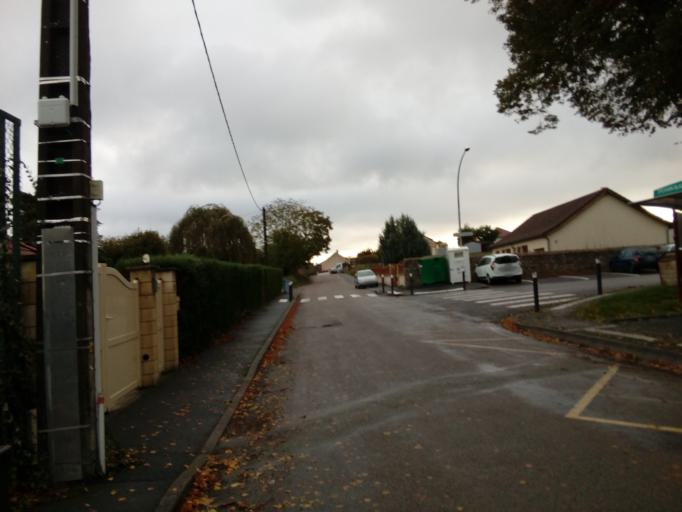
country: FR
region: Limousin
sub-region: Departement de la Creuse
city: Gueret
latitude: 46.1782
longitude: 1.8636
